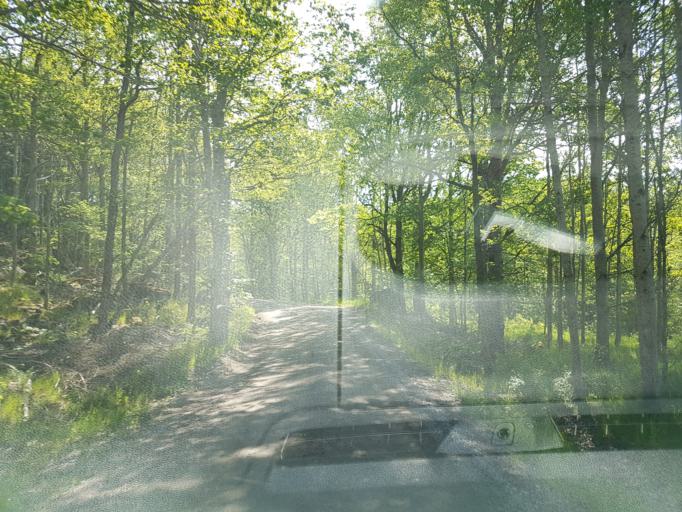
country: SE
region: OEstergoetland
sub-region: Atvidabergs Kommun
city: Atvidaberg
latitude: 58.1850
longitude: 16.1199
